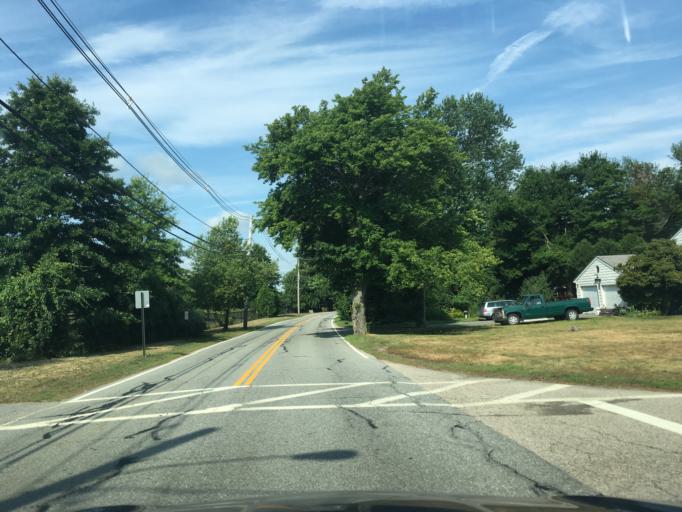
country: US
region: Rhode Island
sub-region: Kent County
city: East Greenwich
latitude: 41.6095
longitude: -71.4372
